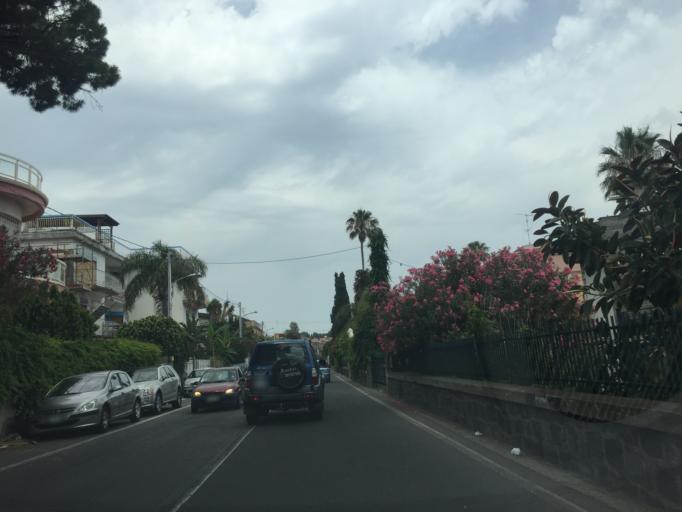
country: IT
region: Sicily
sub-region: Catania
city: Vambolieri
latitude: 37.5702
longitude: 15.1646
